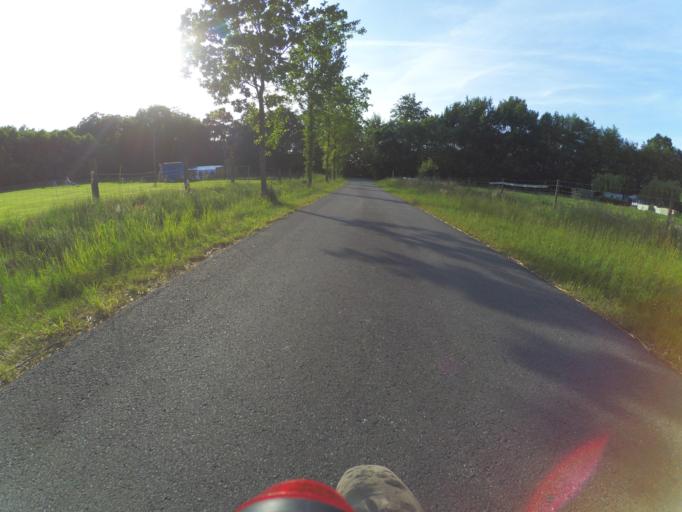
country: DE
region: North Rhine-Westphalia
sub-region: Regierungsbezirk Munster
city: Birgte
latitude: 52.2729
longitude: 7.6595
